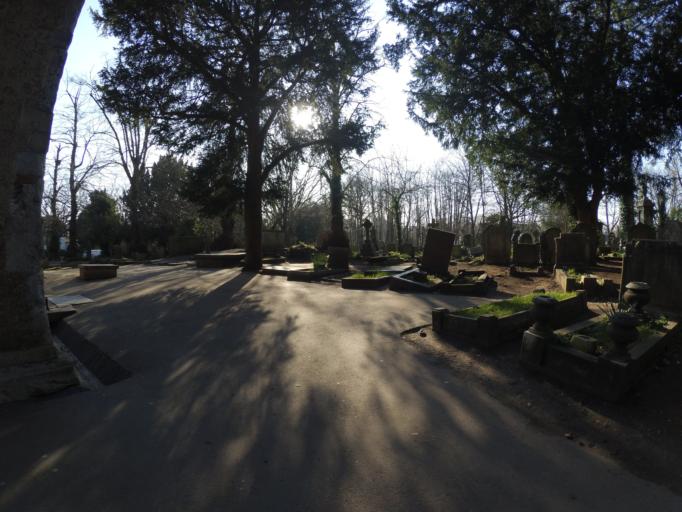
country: GB
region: England
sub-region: Greater London
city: Wembley
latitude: 51.5678
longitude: -0.2611
